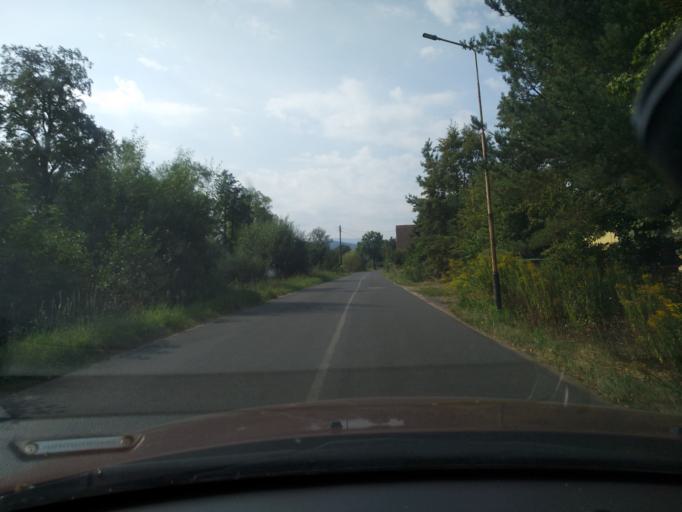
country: PL
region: Lower Silesian Voivodeship
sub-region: Powiat jeleniogorski
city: Stara Kamienica
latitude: 50.9255
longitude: 15.5733
